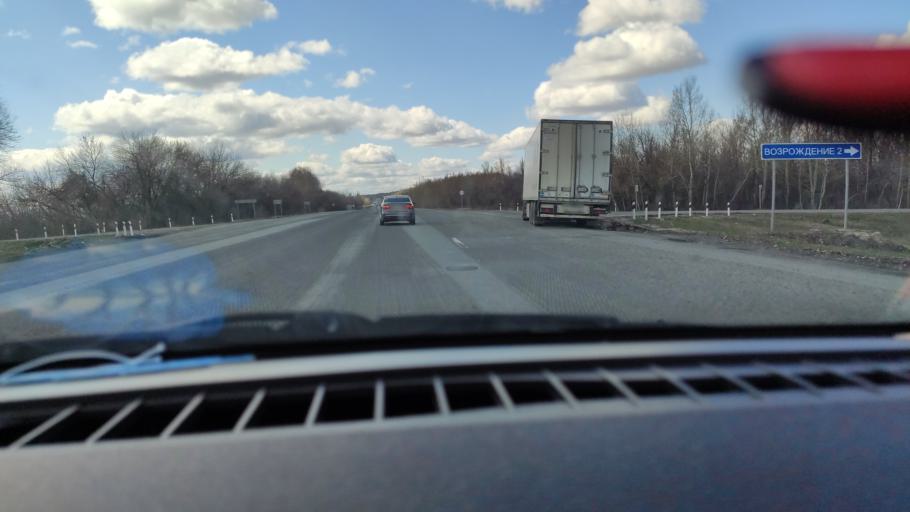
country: RU
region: Saratov
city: Dukhovnitskoye
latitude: 52.6597
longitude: 48.2095
